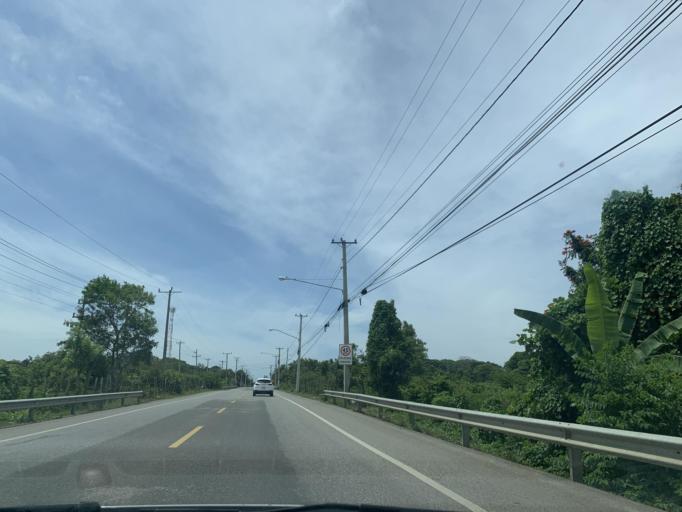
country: DO
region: Puerto Plata
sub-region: Puerto Plata
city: Puerto Plata
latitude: 19.7516
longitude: -70.6403
